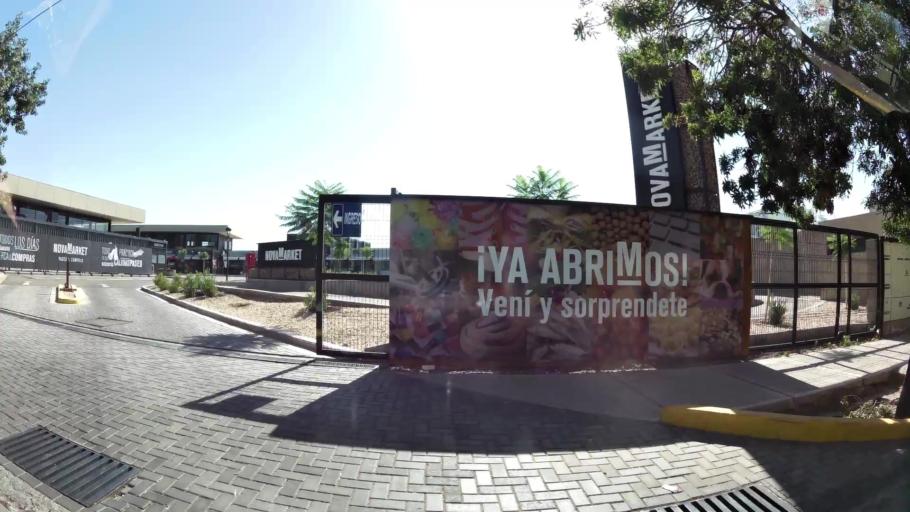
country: AR
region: Mendoza
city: Villa Nueva
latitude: -32.9079
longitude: -68.7905
